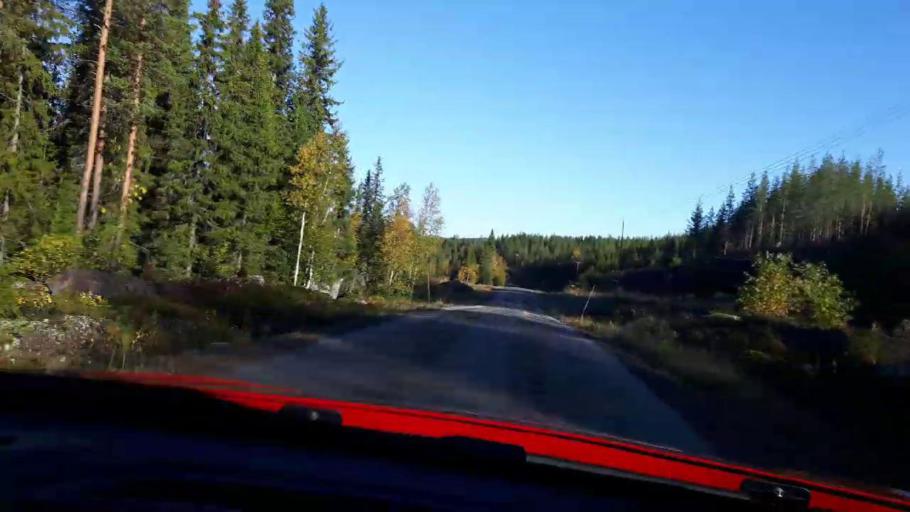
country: SE
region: Jaemtland
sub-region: Stroemsunds Kommun
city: Stroemsund
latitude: 64.3697
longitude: 15.1580
